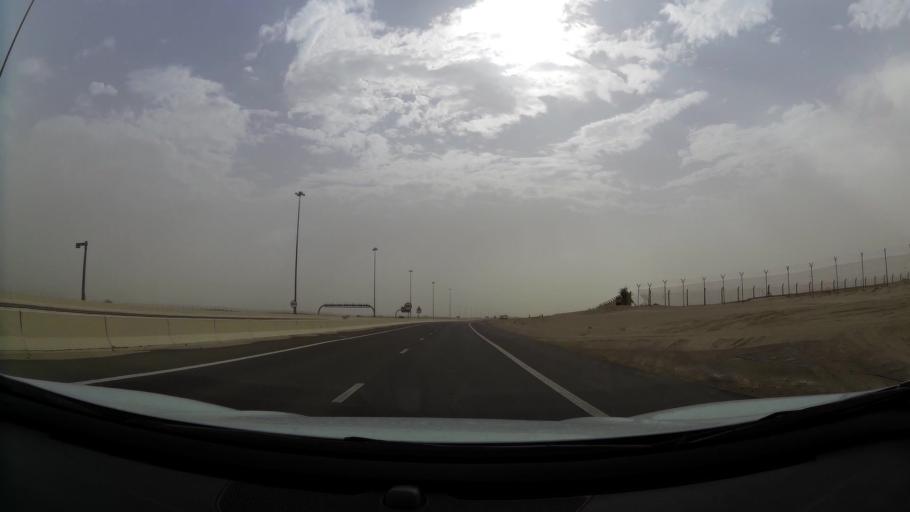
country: AE
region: Abu Dhabi
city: Abu Dhabi
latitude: 24.4804
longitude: 54.6592
